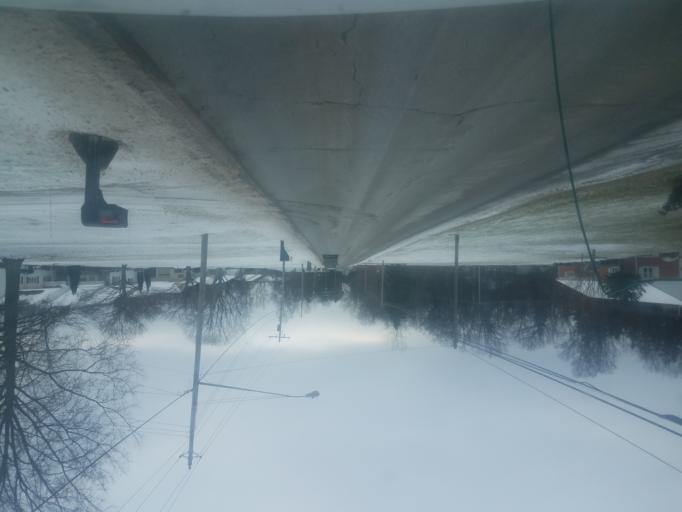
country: US
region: Ohio
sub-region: Richland County
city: Ontario
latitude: 40.7240
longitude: -82.5553
